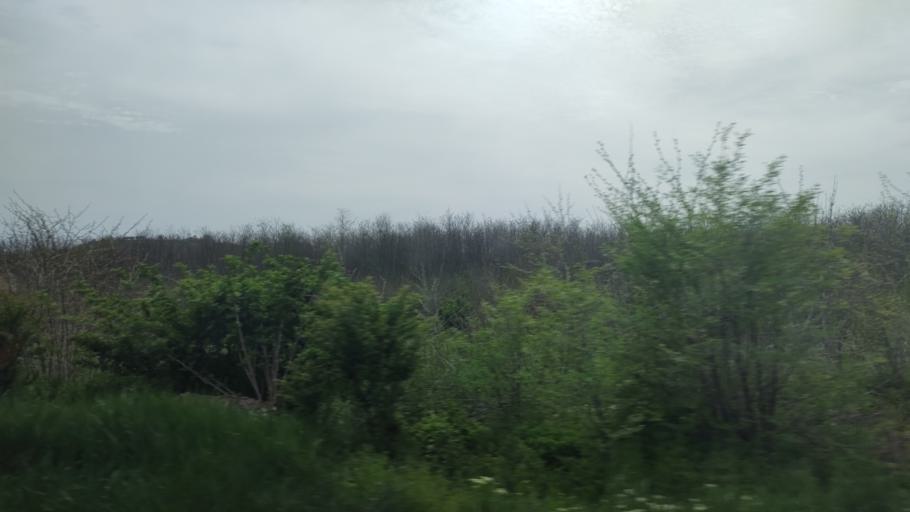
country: RO
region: Constanta
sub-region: Oras Murfatlar
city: Murfatlar
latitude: 44.1696
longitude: 28.3971
